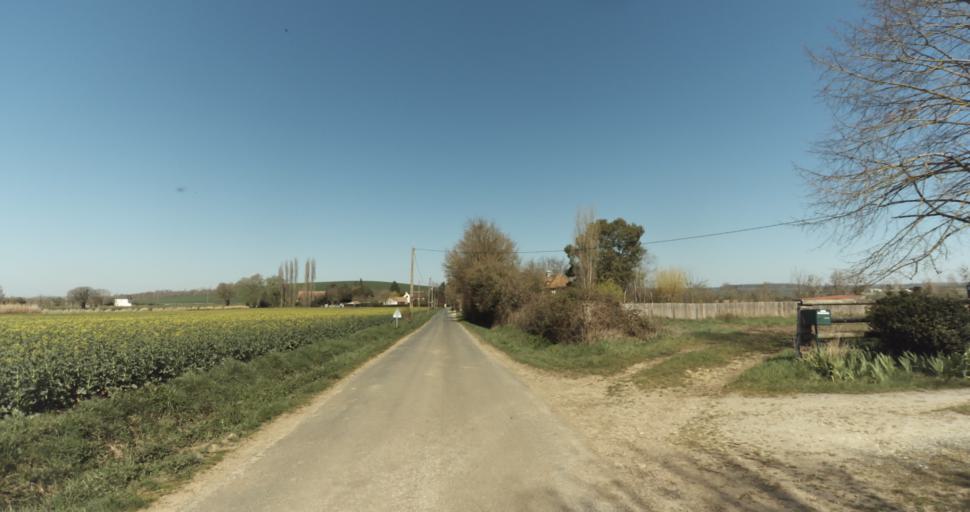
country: FR
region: Lower Normandy
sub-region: Departement du Calvados
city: Saint-Pierre-sur-Dives
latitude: 49.0122
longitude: 0.0139
